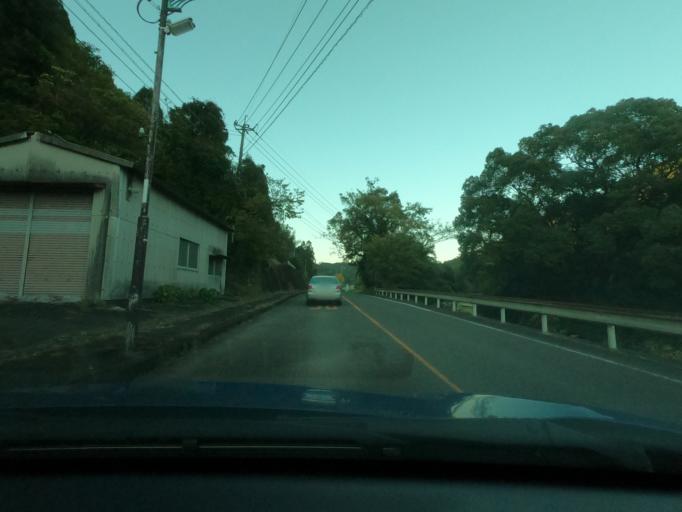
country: JP
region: Kagoshima
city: Satsumasendai
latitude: 31.8023
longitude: 130.4804
